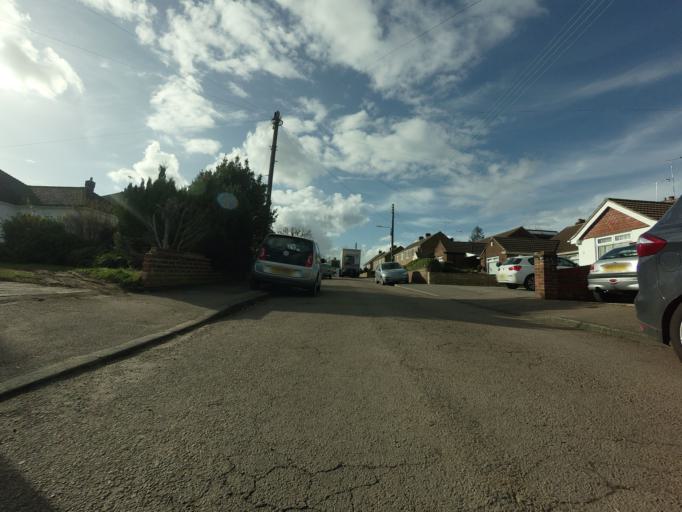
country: GB
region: England
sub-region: Kent
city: Swanley
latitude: 51.4001
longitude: 0.1800
